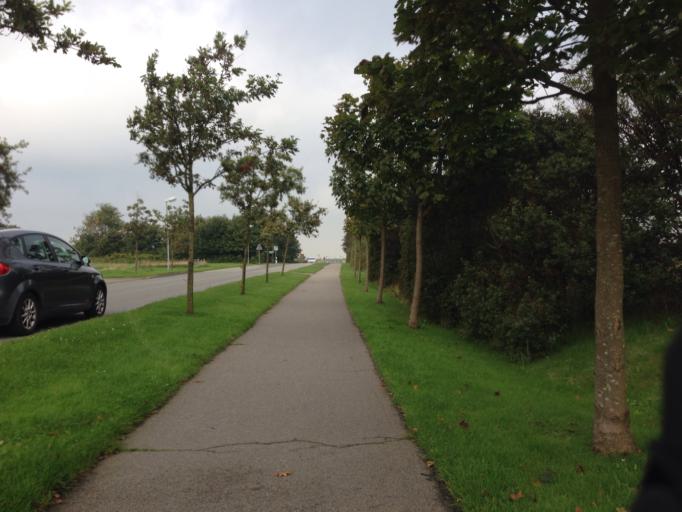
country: DE
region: Schleswig-Holstein
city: Wrixum
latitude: 54.7007
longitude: 8.5451
